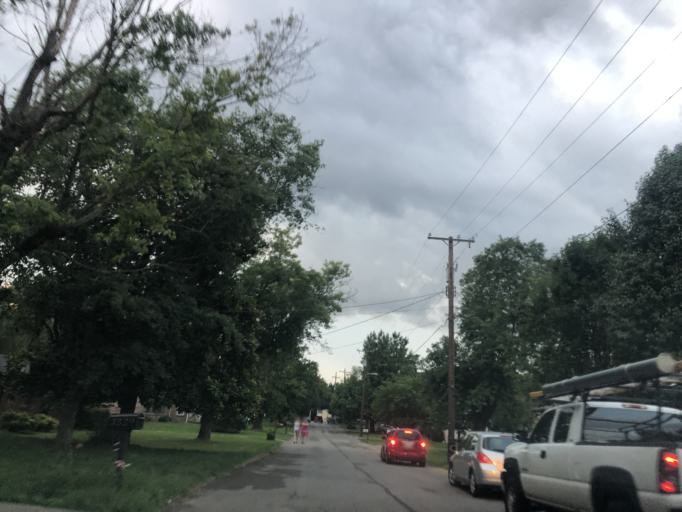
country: US
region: Tennessee
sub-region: Davidson County
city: Lakewood
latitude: 36.1513
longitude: -86.6347
